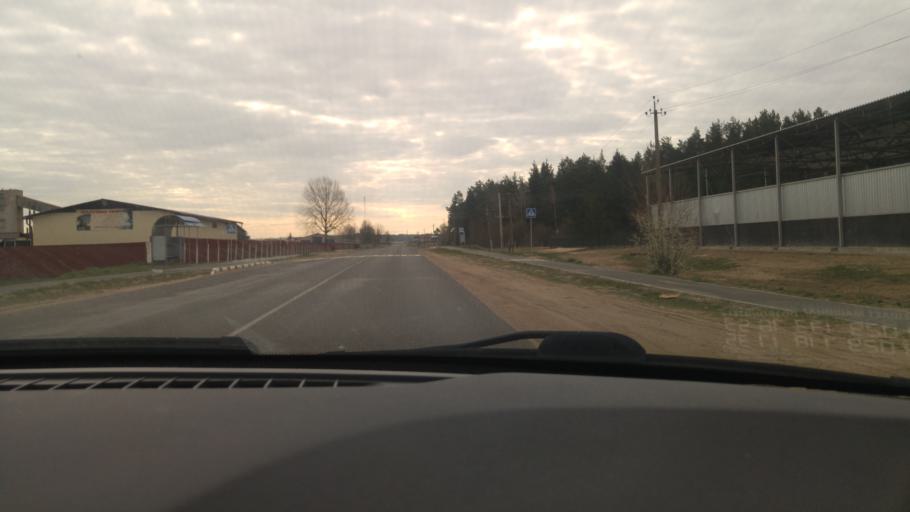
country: BY
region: Minsk
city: Chervyen'
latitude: 53.6979
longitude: 28.4240
